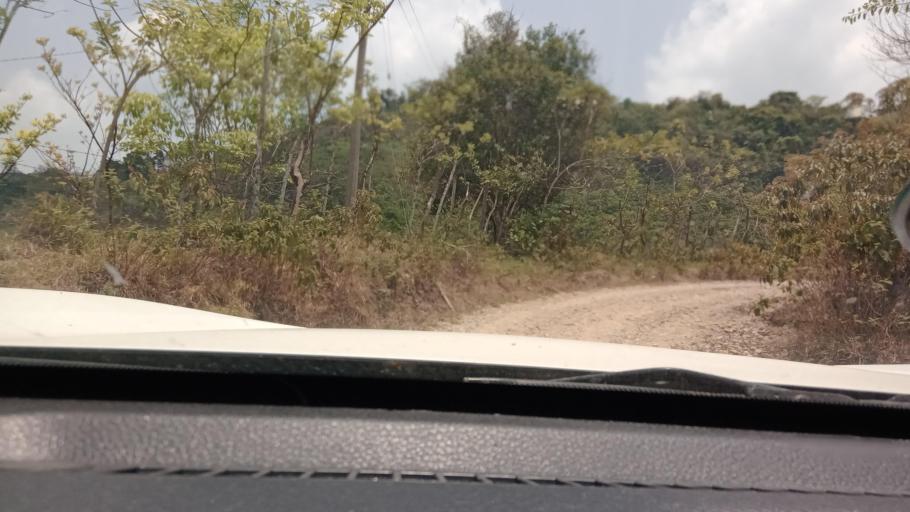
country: MX
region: Tabasco
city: Chontalpa
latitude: 17.5500
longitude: -93.7402
